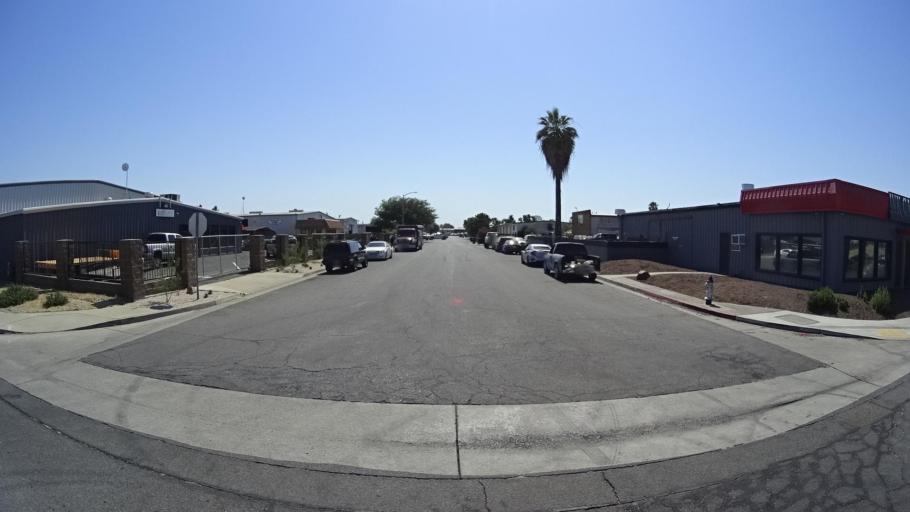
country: US
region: California
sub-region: Fresno County
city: Tarpey Village
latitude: 36.7880
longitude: -119.7317
